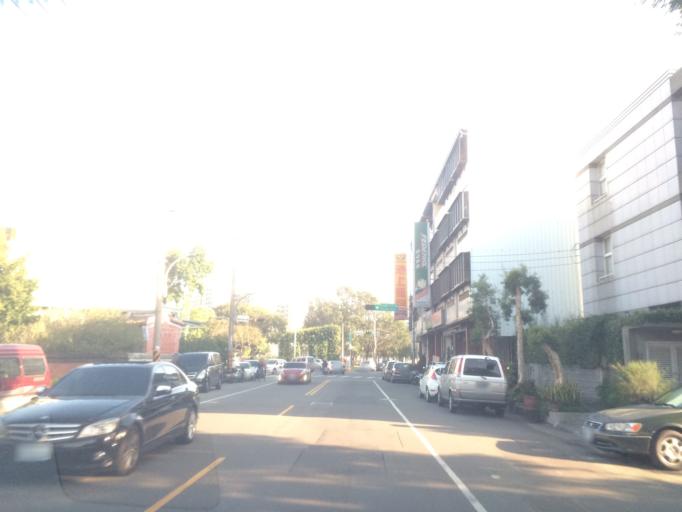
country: TW
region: Taiwan
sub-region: Taichung City
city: Taichung
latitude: 24.1909
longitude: 120.6844
